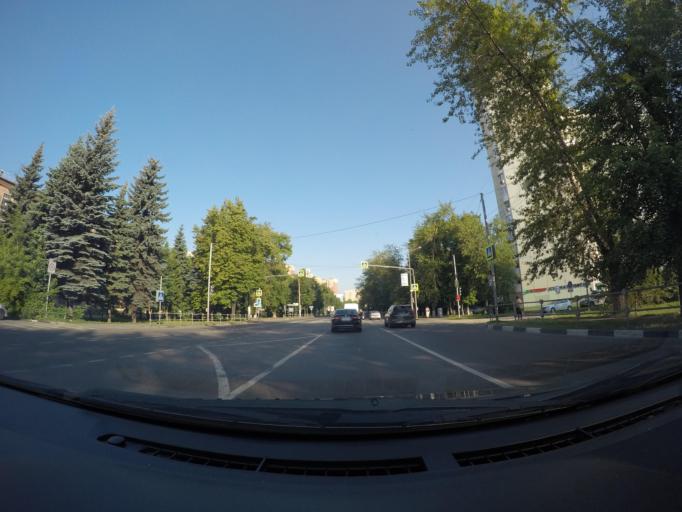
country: RU
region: Moskovskaya
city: Lyubertsy
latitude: 55.6861
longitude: 37.8775
